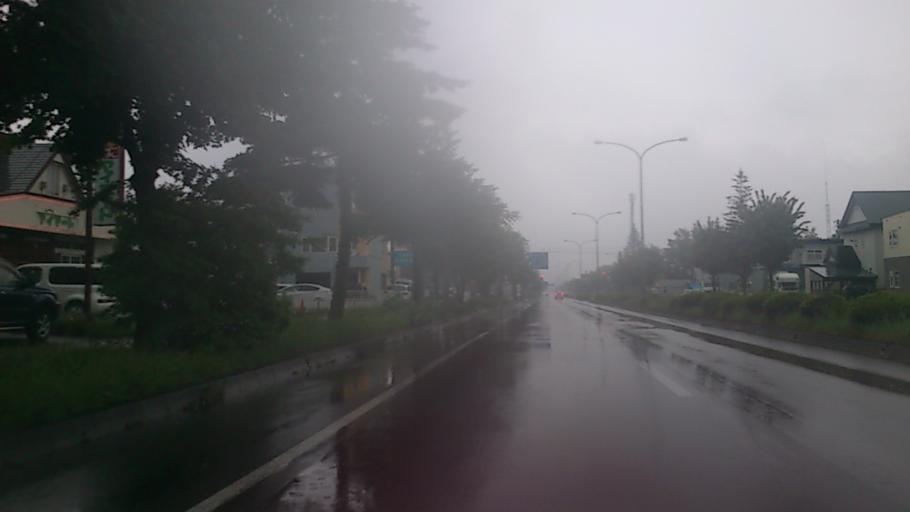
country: JP
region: Hokkaido
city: Obihiro
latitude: 42.9094
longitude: 143.1317
